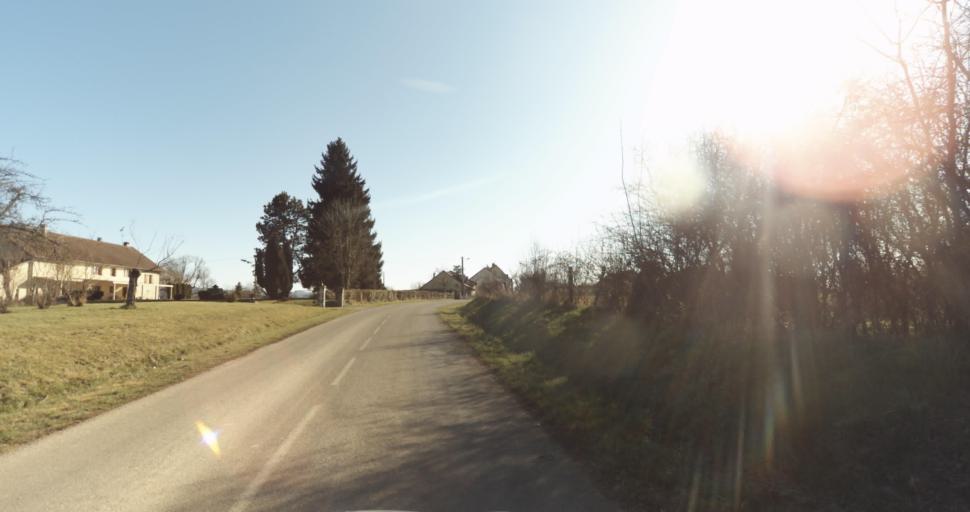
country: FR
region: Franche-Comte
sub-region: Departement du Jura
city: Montmorot
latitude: 46.6865
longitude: 5.4998
